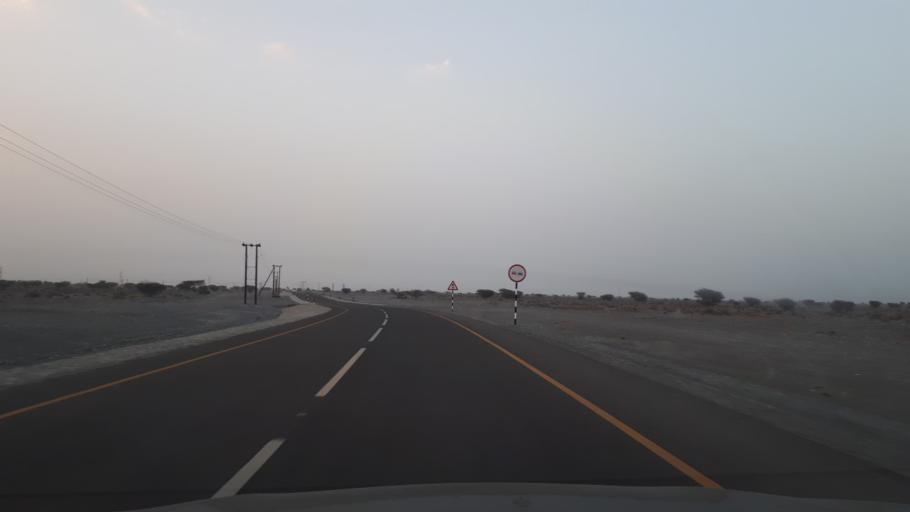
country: OM
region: Al Batinah
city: Rustaq
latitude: 23.5846
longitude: 57.5828
